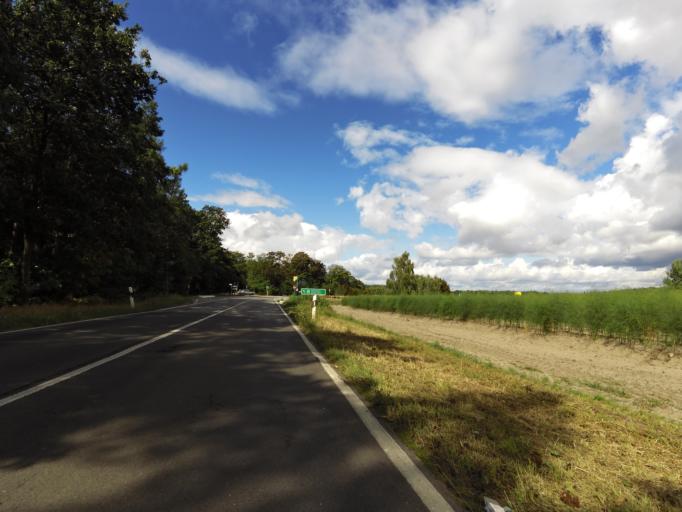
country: DE
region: Berlin
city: Marienfelde
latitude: 52.3675
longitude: 13.3639
